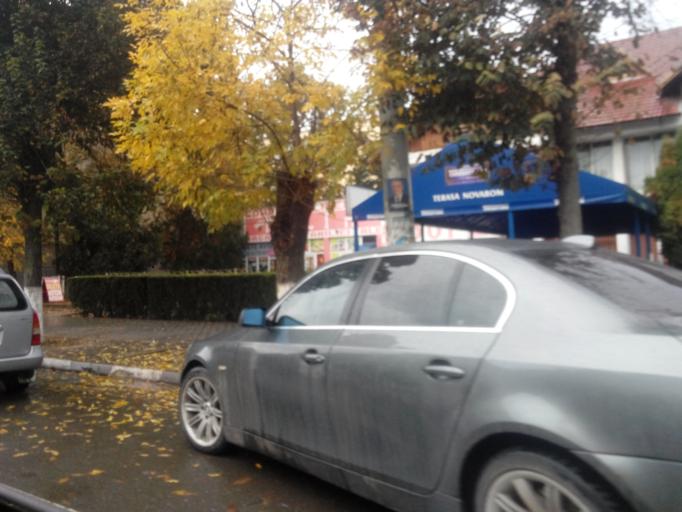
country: RO
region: Ialomita
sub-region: Municipiul Urziceni
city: Urziceni
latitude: 44.7143
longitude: 26.6427
